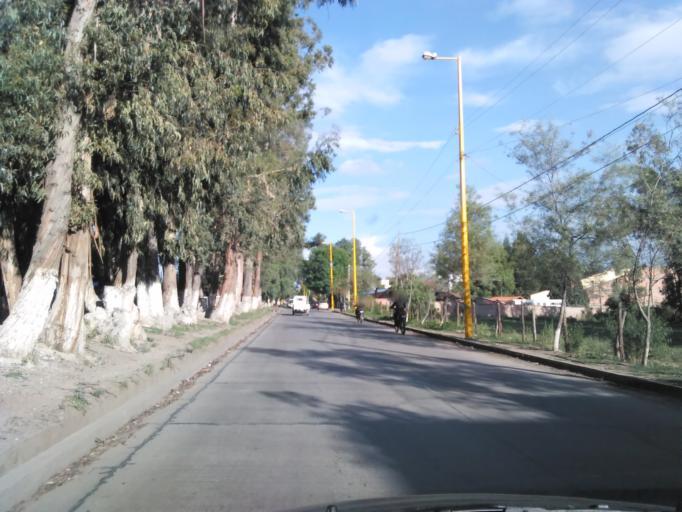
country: BO
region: Cochabamba
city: Cochabamba
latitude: -17.3432
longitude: -66.2094
